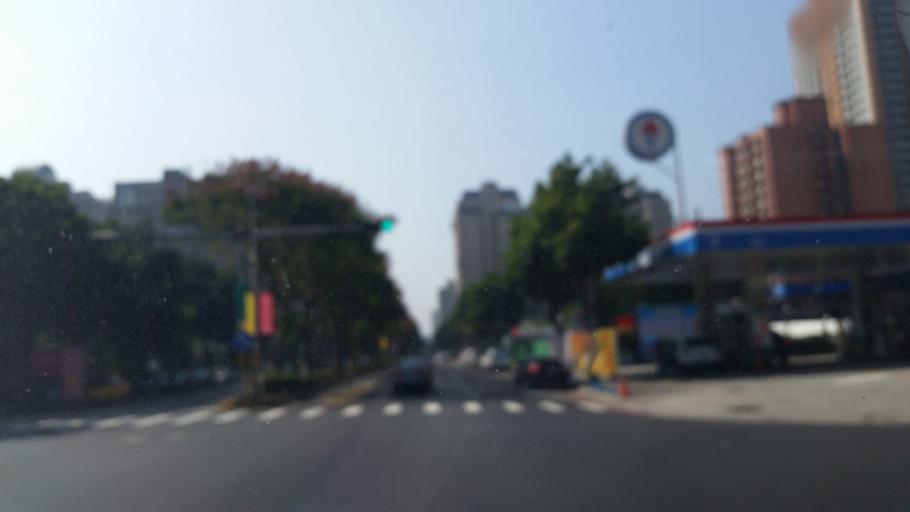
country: TW
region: Taiwan
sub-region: Taoyuan
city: Taoyuan
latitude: 25.0752
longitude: 121.3724
